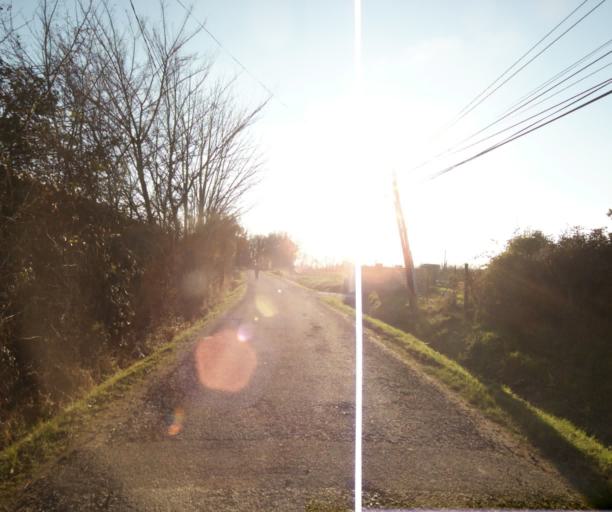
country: FR
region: Midi-Pyrenees
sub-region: Departement du Tarn-et-Garonne
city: Moissac
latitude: 44.1422
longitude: 1.1408
